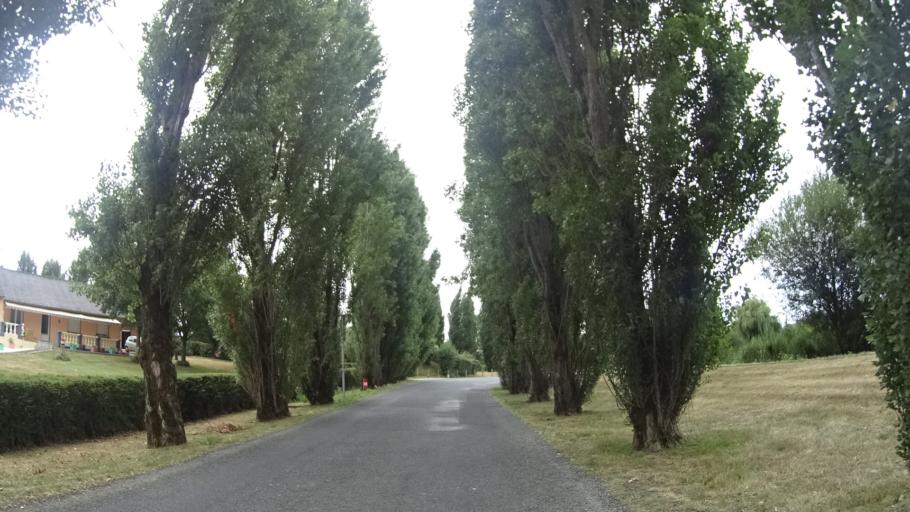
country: FR
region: Pays de la Loire
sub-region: Departement de la Loire-Atlantique
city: Fay-de-Bretagne
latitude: 47.4144
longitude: -1.7860
